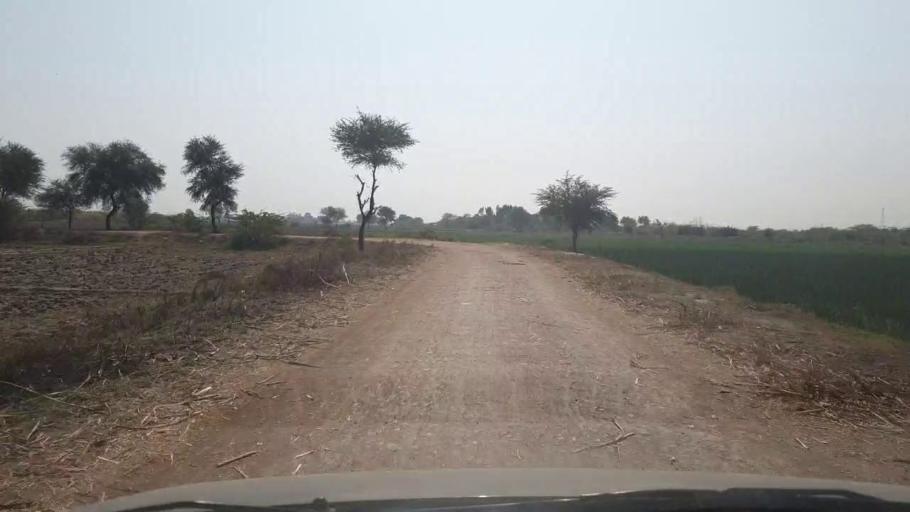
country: PK
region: Sindh
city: Mirwah Gorchani
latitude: 25.3052
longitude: 69.1573
